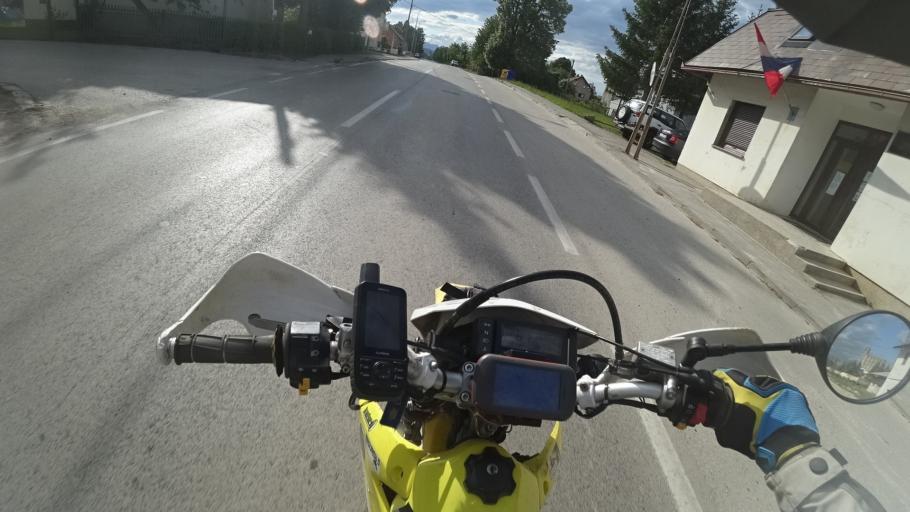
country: HR
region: Licko-Senjska
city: Gospic
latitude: 44.5354
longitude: 15.3940
